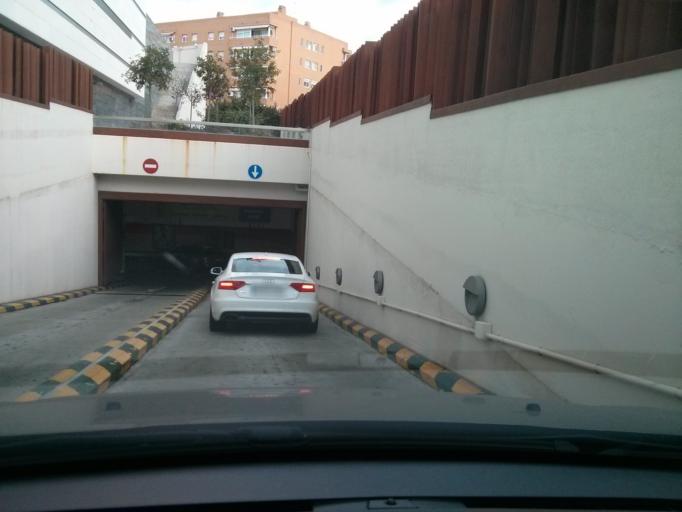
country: ES
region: Catalonia
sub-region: Provincia de Tarragona
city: Tarragona
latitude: 41.1209
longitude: 1.2423
